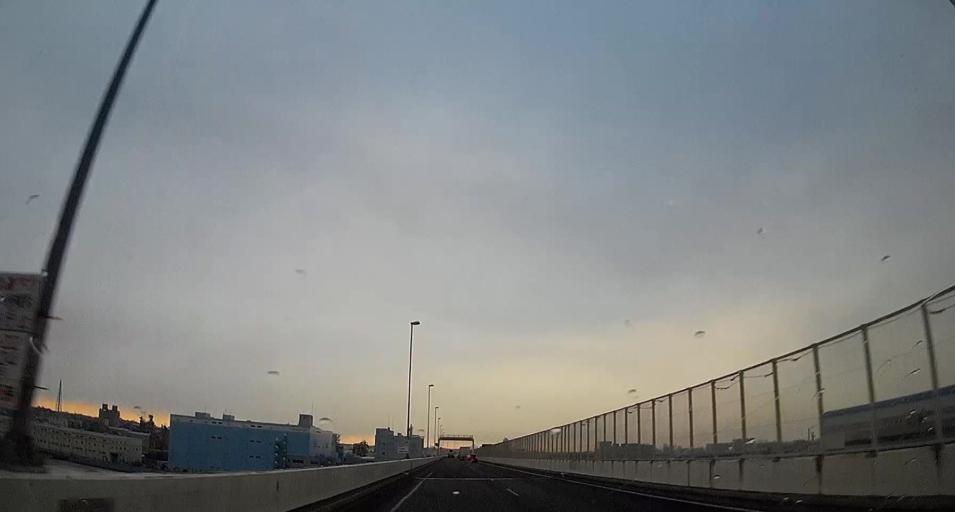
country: JP
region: Kanagawa
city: Yokohama
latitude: 35.4753
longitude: 139.6753
